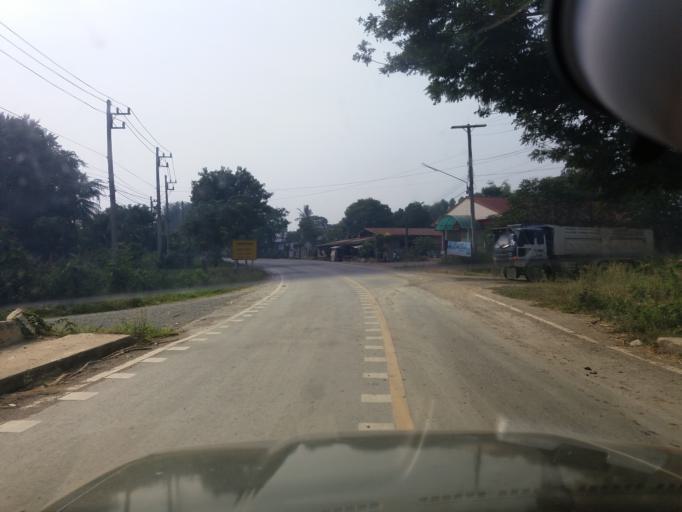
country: TH
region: Sing Buri
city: Bang Racham
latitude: 14.9083
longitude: 100.2221
